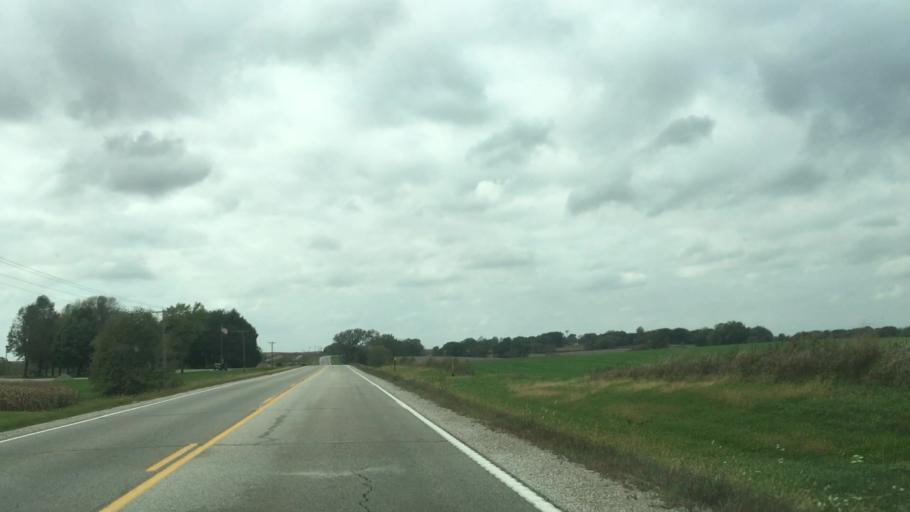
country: US
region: Minnesota
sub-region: Fillmore County
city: Preston
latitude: 43.7354
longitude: -92.1125
